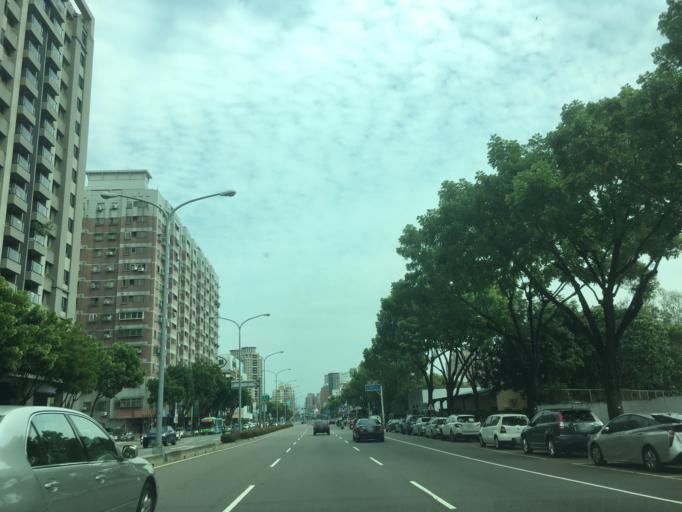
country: TW
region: Taiwan
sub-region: Taichung City
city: Taichung
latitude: 24.1197
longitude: 120.6509
